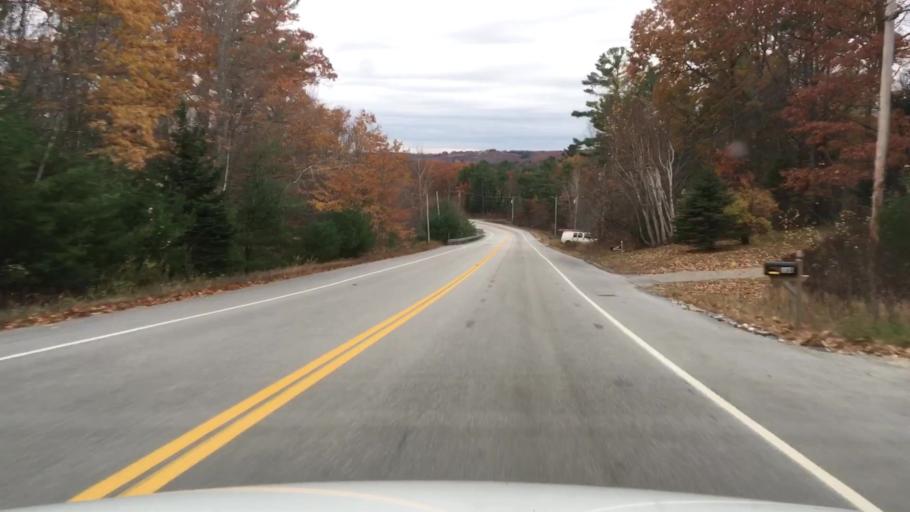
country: US
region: Maine
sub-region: Hancock County
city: Orland
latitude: 44.5557
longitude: -68.6963
